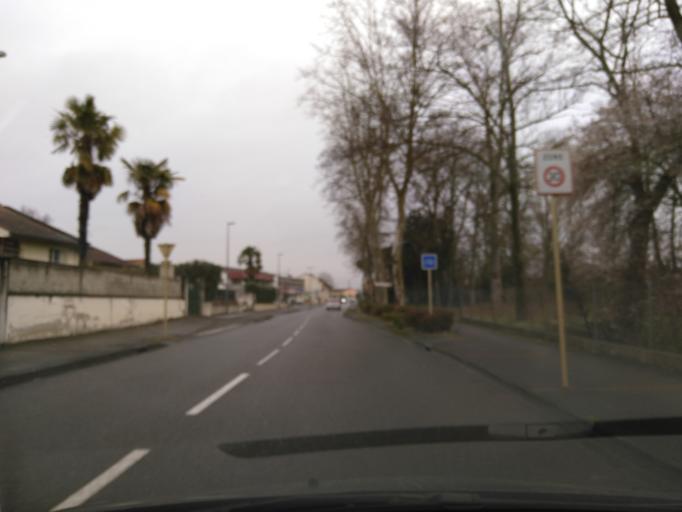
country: FR
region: Midi-Pyrenees
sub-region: Departement de la Haute-Garonne
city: Carbonne
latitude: 43.2955
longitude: 1.2169
